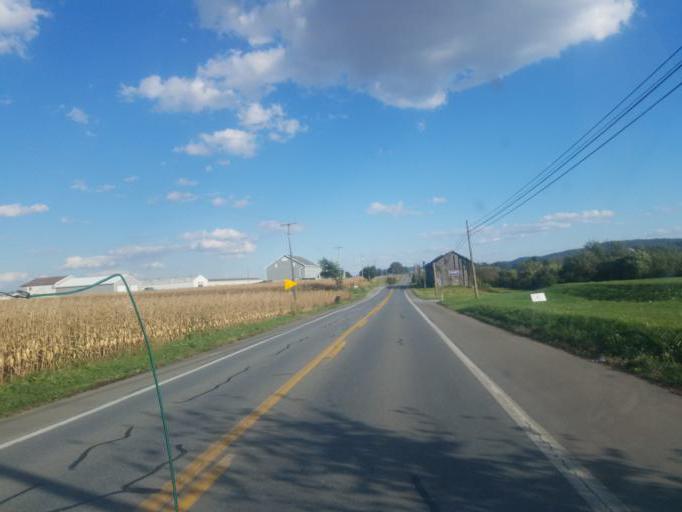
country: US
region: Pennsylvania
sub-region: Lancaster County
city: Bainbridge
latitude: 40.0722
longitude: -76.6338
